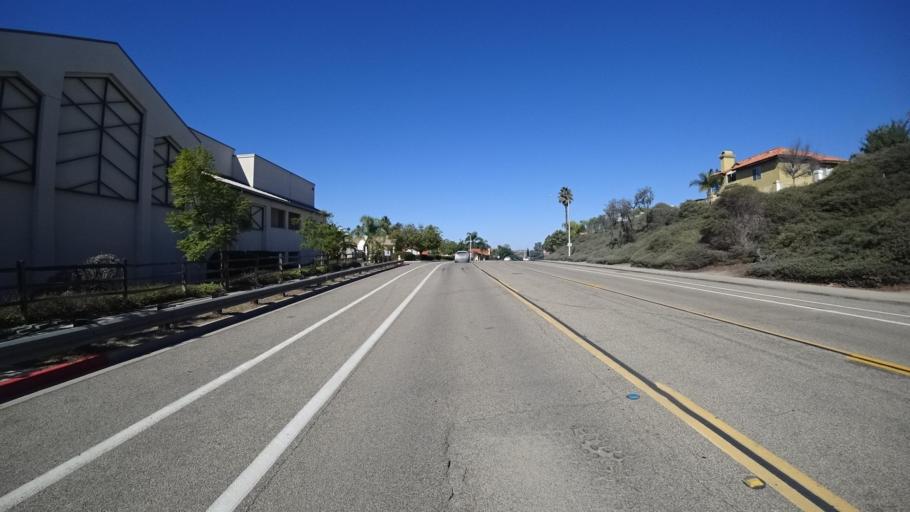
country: US
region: California
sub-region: San Diego County
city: Bonita
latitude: 32.6589
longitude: -116.9969
